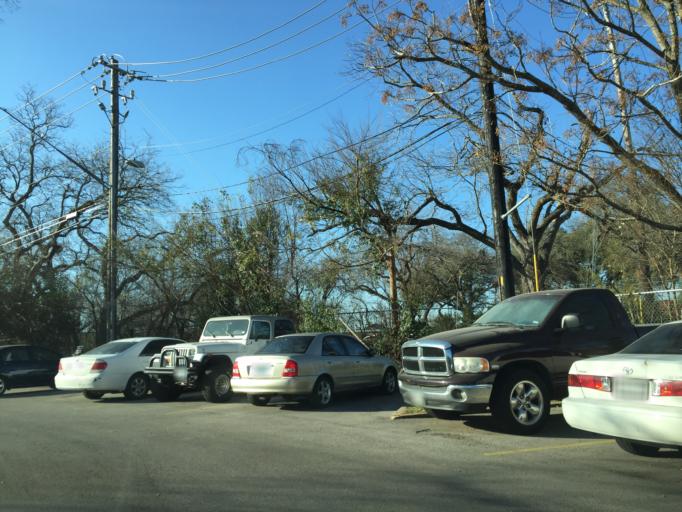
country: US
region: Texas
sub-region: Williamson County
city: Jollyville
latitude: 30.4376
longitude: -97.7697
